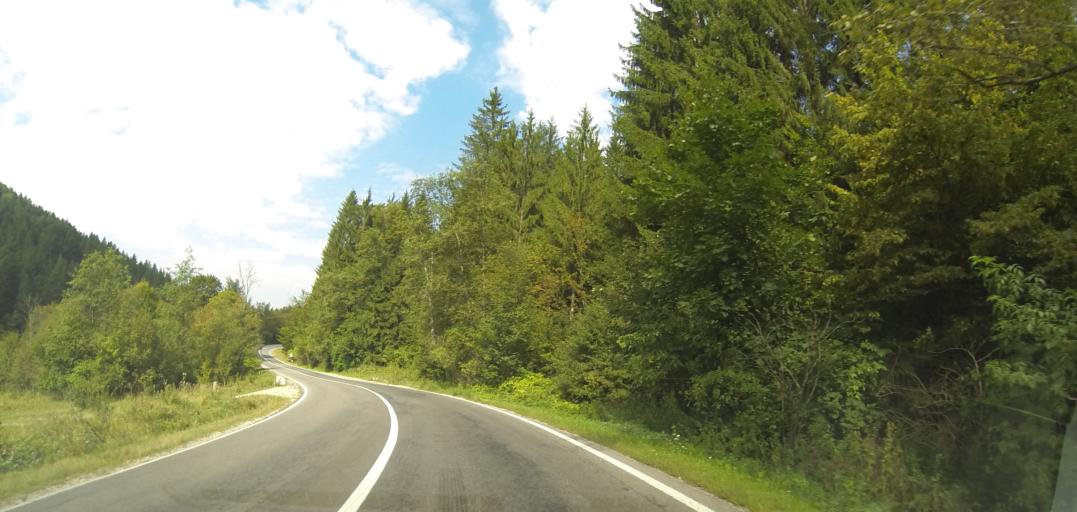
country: RO
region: Brasov
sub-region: Comuna Tarlungeni
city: Zizin
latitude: 45.5510
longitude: 25.8126
